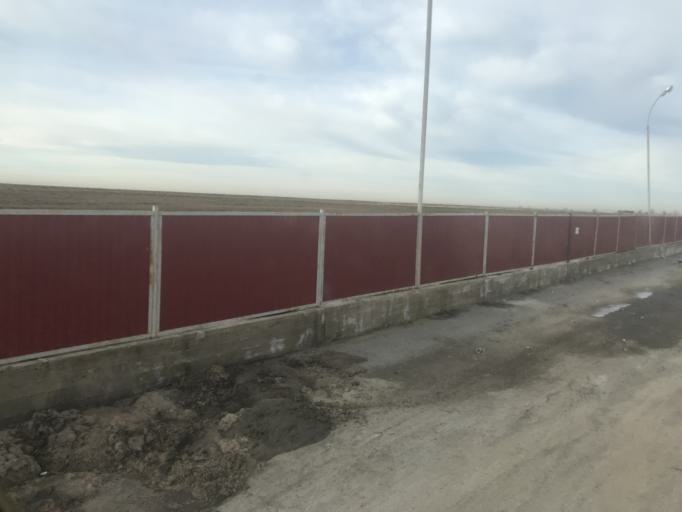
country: KZ
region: Ongtustik Qazaqstan
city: Shymkent
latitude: 42.4618
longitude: 69.5750
